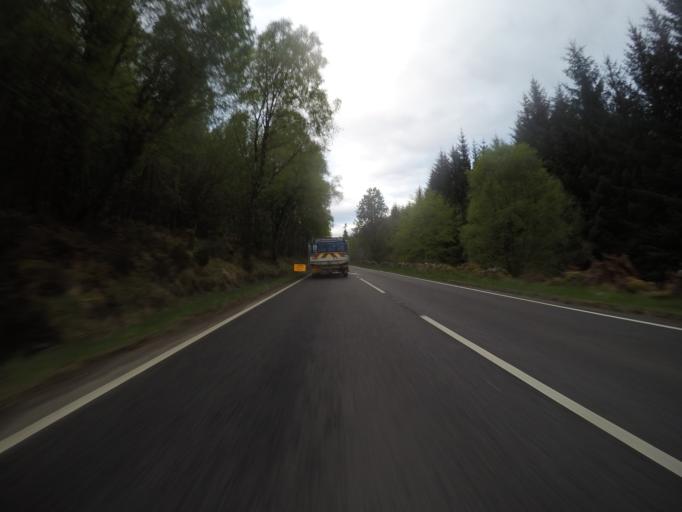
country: GB
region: Scotland
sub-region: Highland
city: Spean Bridge
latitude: 57.1193
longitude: -4.7006
